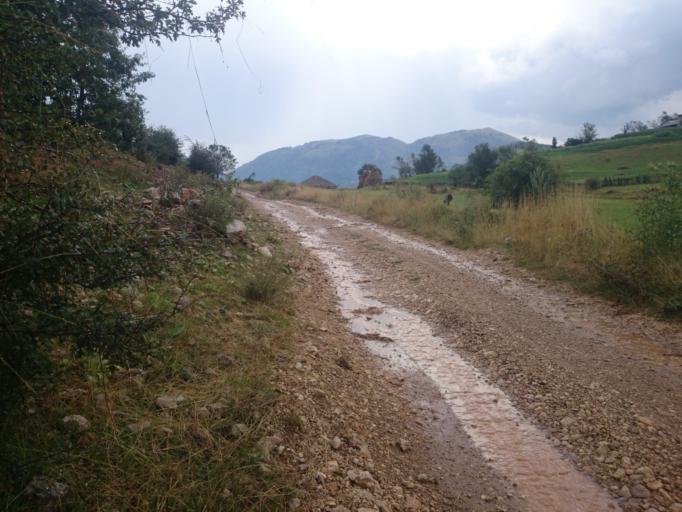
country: AL
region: Diber
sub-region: Rrethi i Dibres
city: Fushe-Lure
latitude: 41.8362
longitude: 20.1753
